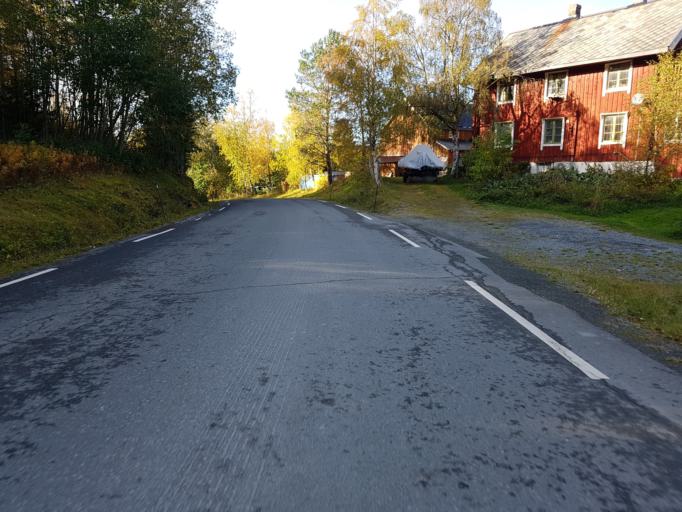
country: NO
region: Sor-Trondelag
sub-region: Klaebu
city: Klaebu
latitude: 63.3399
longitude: 10.5742
